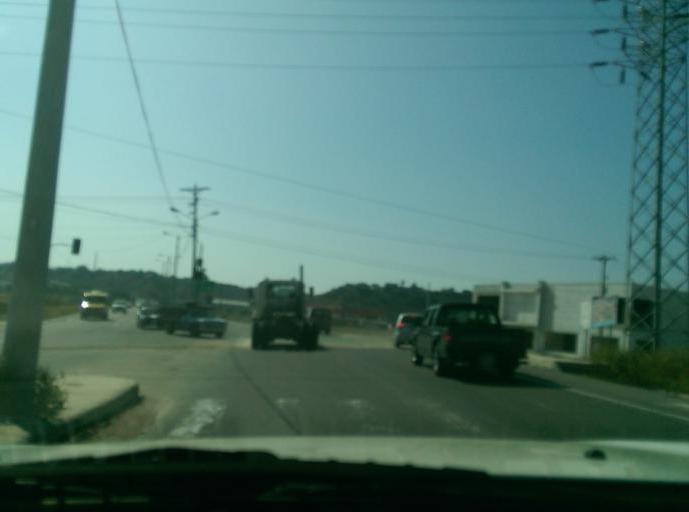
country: EC
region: Manabi
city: Manta
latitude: -0.9658
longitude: -80.7333
